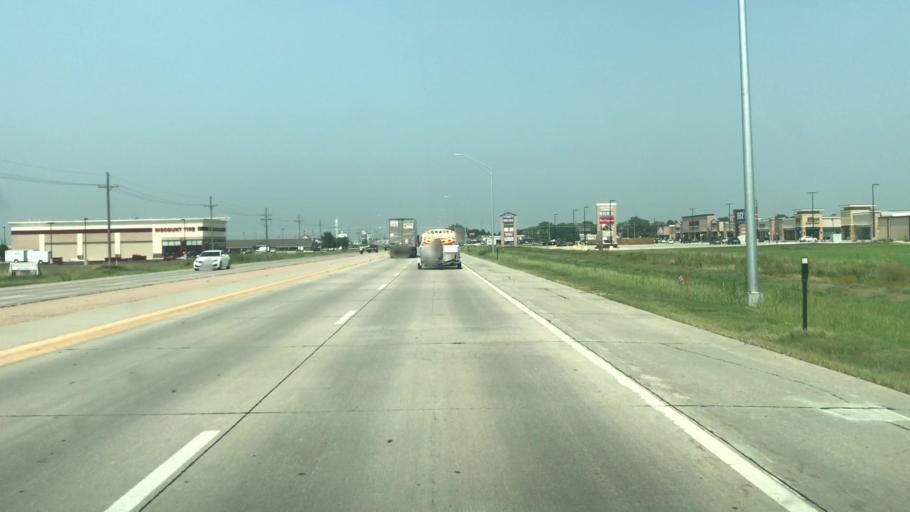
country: US
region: Nebraska
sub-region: Hall County
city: Grand Island
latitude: 40.9410
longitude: -98.3834
